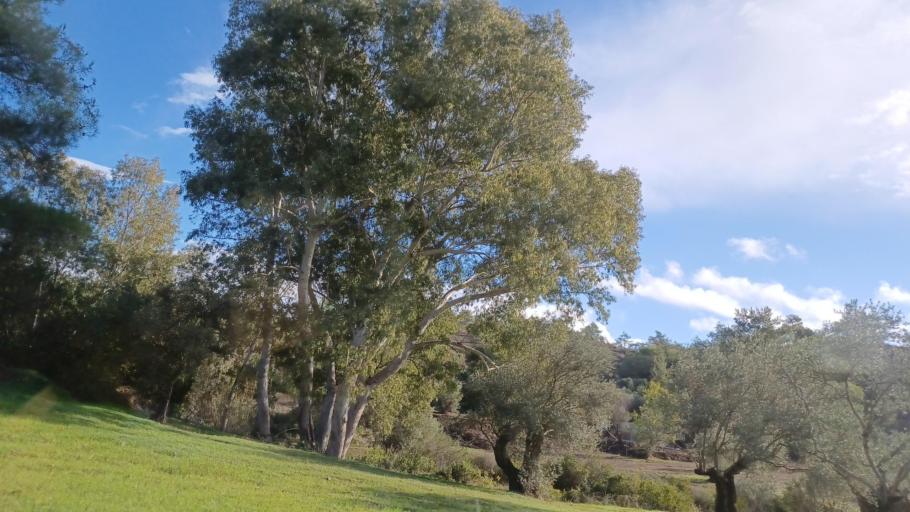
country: CY
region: Lefkosia
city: Lythrodontas
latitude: 34.9354
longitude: 33.2978
